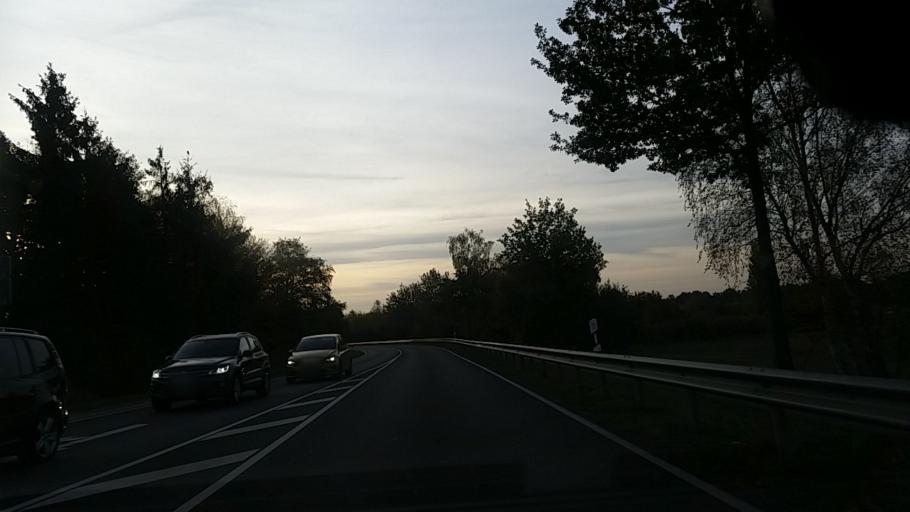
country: DE
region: Lower Saxony
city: Wolfsburg
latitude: 52.4377
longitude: 10.8300
